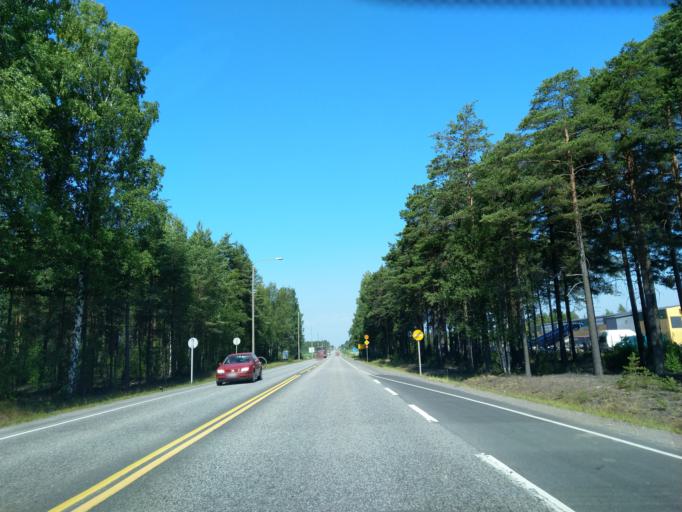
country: FI
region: Satakunta
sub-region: Pori
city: Harjavalta
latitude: 61.3090
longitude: 22.1216
